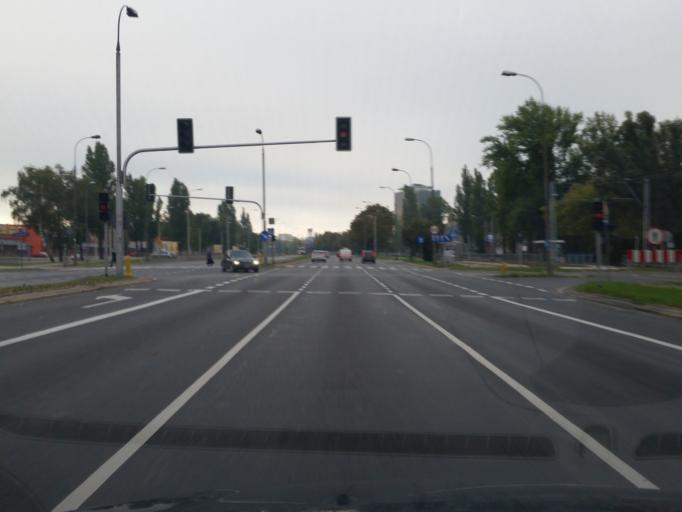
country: PL
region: Masovian Voivodeship
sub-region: Warszawa
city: Zoliborz
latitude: 52.2745
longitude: 21.0144
